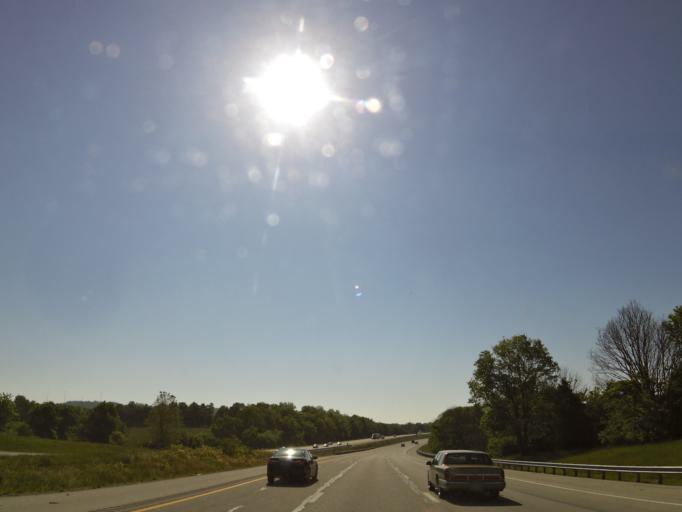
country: US
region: Kentucky
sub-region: Shelby County
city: Shelbyville
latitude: 38.1696
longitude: -85.1474
